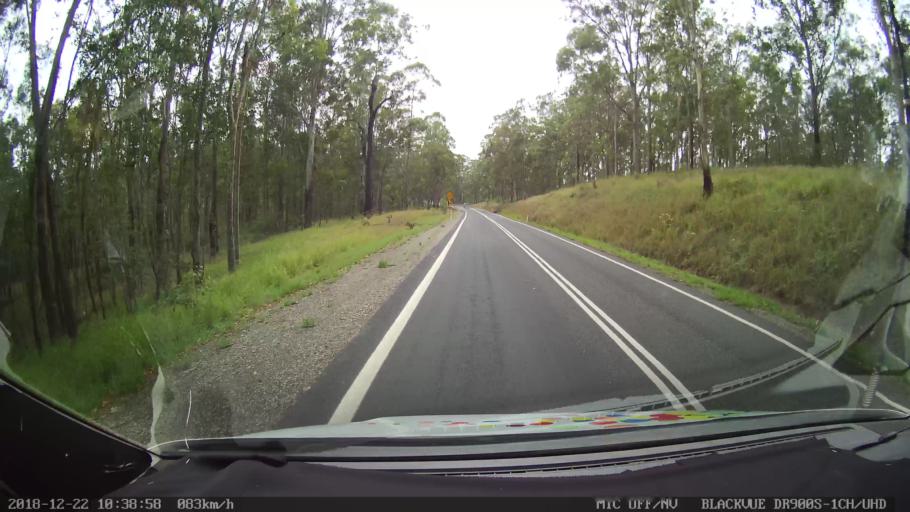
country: AU
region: New South Wales
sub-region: Clarence Valley
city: South Grafton
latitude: -29.6330
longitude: 152.7278
